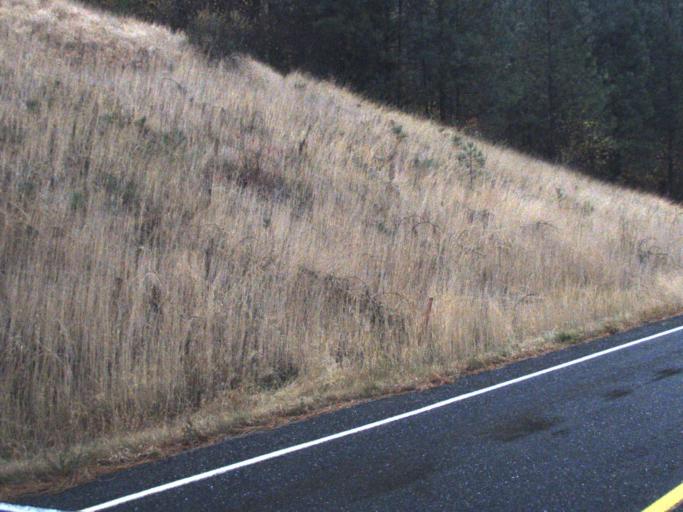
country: US
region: Washington
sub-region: Stevens County
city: Kettle Falls
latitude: 48.5278
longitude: -118.1359
